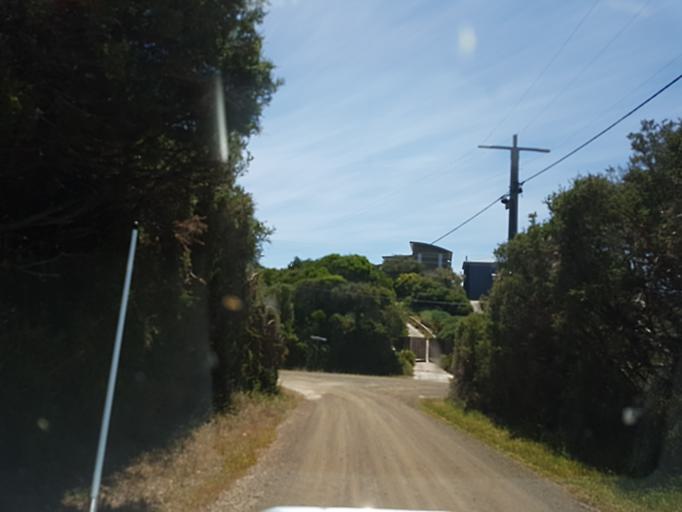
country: AU
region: Victoria
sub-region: Bass Coast
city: North Wonthaggi
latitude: -38.6999
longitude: 145.8262
